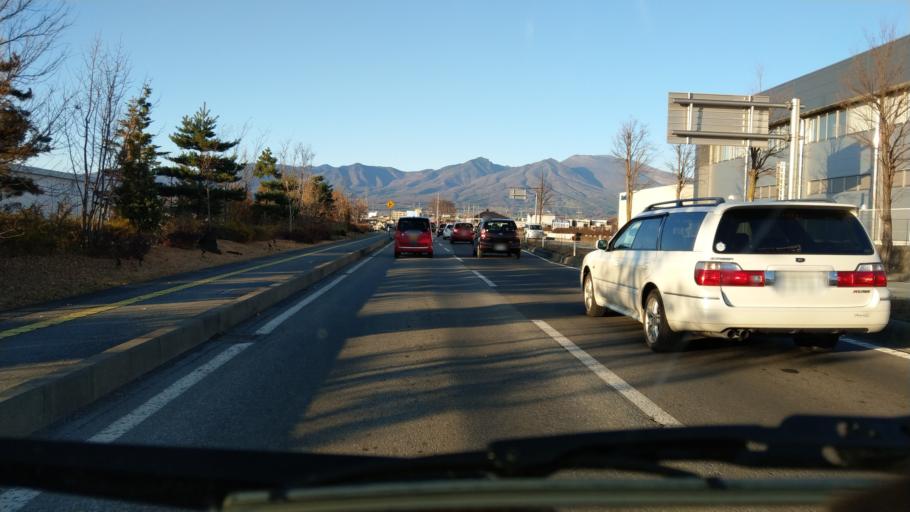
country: JP
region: Nagano
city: Saku
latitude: 36.2572
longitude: 138.4678
